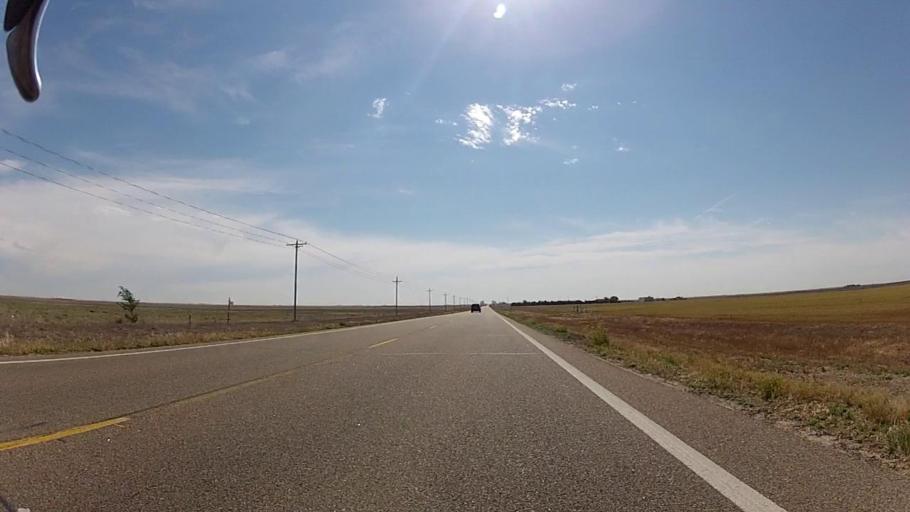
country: US
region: Kansas
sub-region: Grant County
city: Ulysses
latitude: 37.5618
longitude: -101.2902
